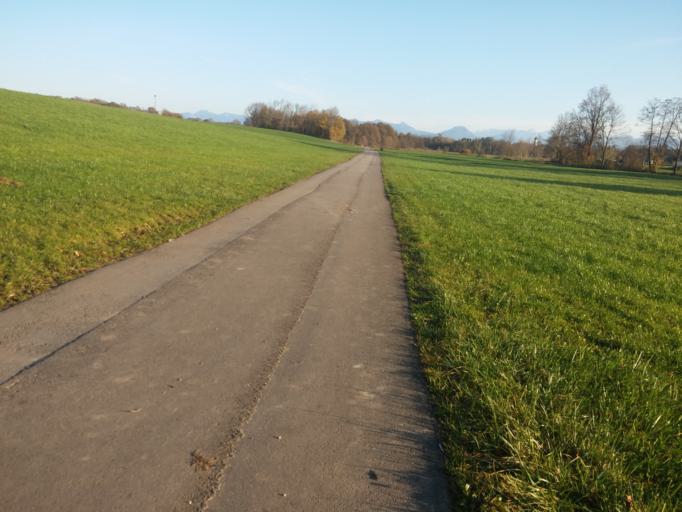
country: DE
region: Bavaria
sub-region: Upper Bavaria
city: Bad Aibling
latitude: 47.8802
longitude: 11.9986
